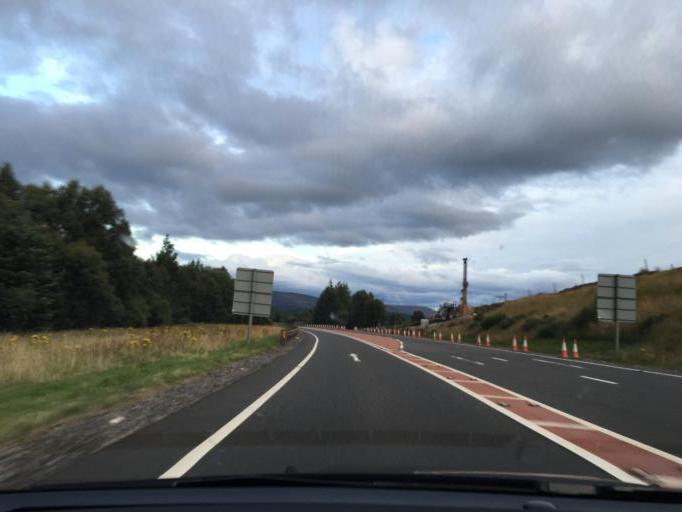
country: GB
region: Scotland
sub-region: Highland
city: Inverness
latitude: 57.3741
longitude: -4.0344
